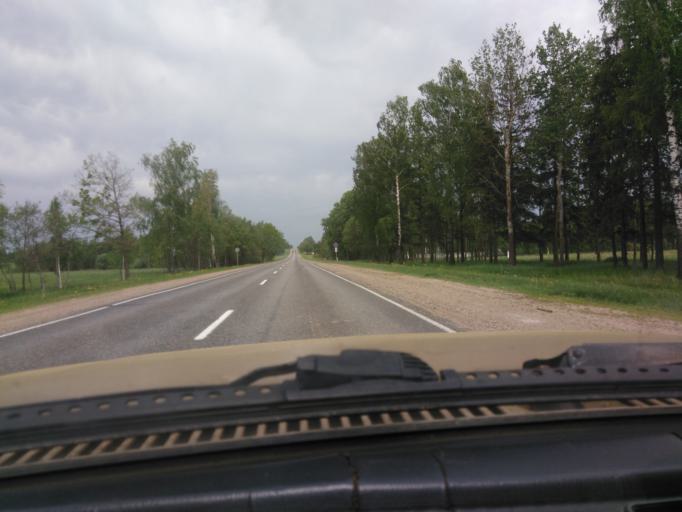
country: BY
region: Mogilev
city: Palykavichy Pyershyya
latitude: 54.0050
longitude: 30.3204
